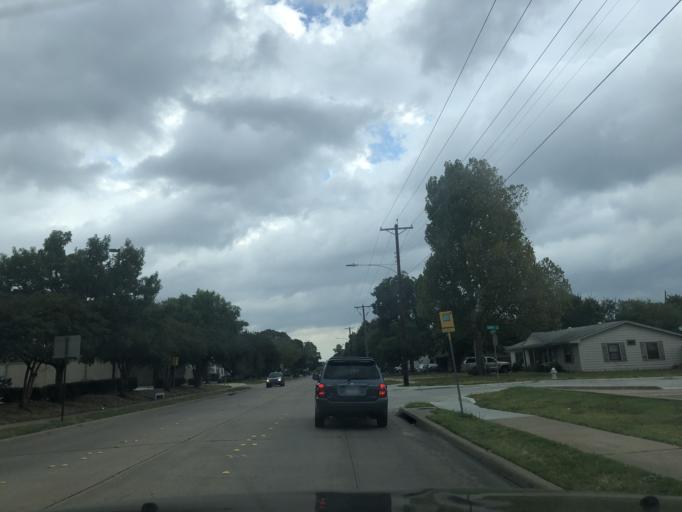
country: US
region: Texas
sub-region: Dallas County
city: Garland
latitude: 32.8809
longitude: -96.6479
